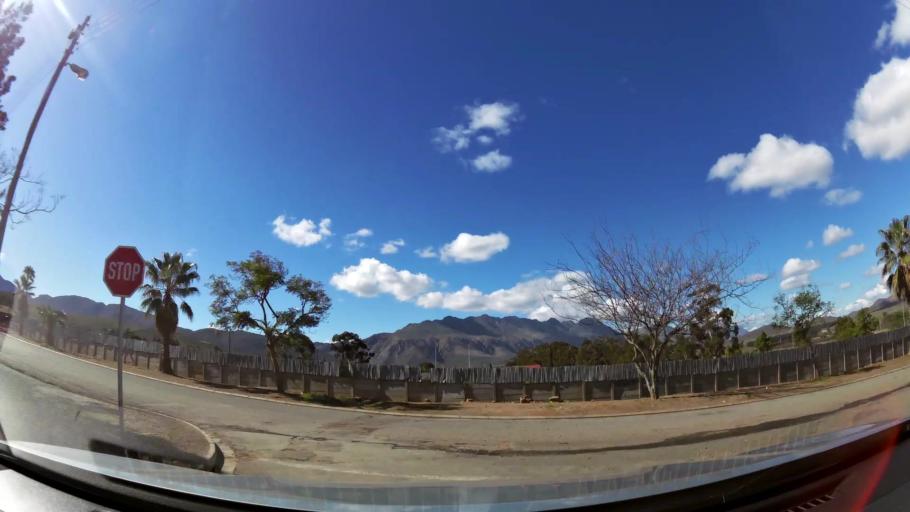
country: ZA
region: Western Cape
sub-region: Cape Winelands District Municipality
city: Ashton
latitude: -33.8349
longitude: 20.0460
